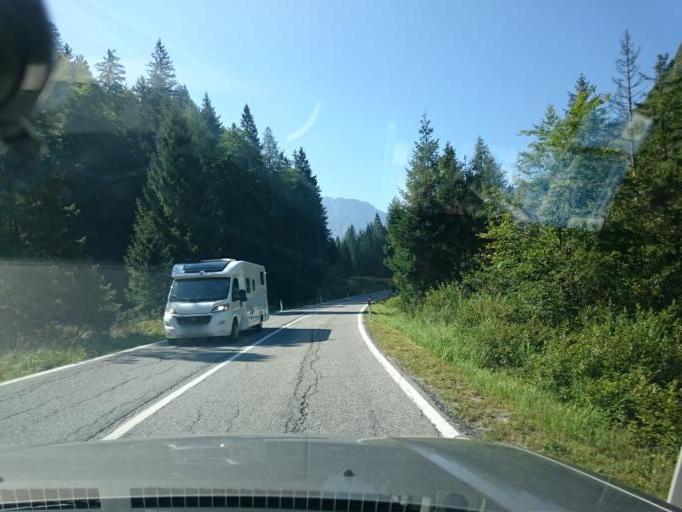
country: IT
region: Friuli Venezia Giulia
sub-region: Provincia di Udine
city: Tarvisio
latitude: 46.4505
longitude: 13.5751
